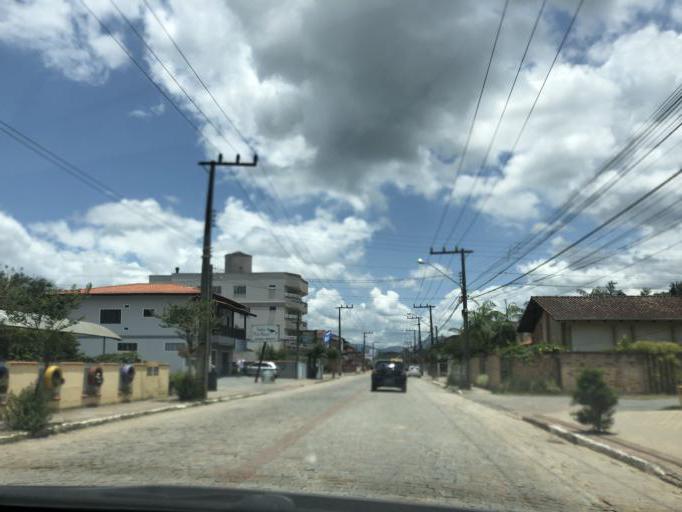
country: BR
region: Santa Catarina
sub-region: Jaragua Do Sul
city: Jaragua do Sul
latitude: -26.5165
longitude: -49.1308
